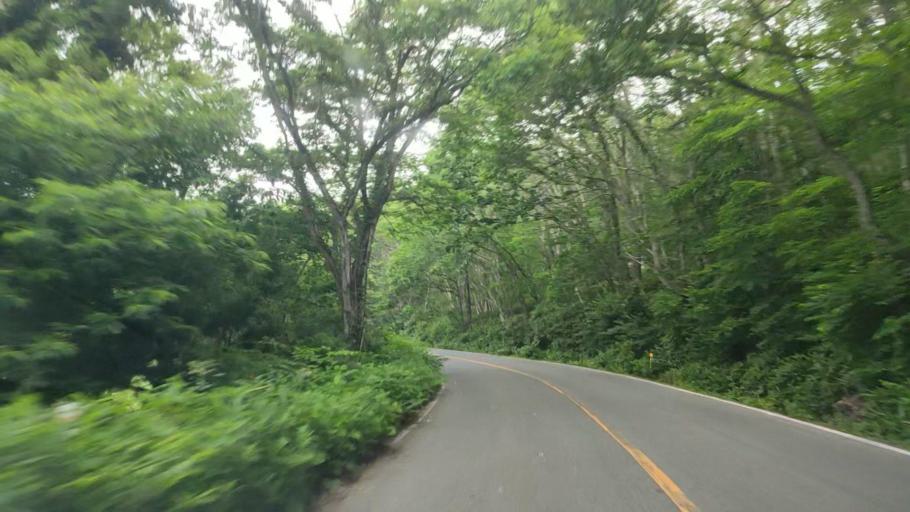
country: JP
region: Tottori
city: Yonago
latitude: 35.3320
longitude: 133.5744
